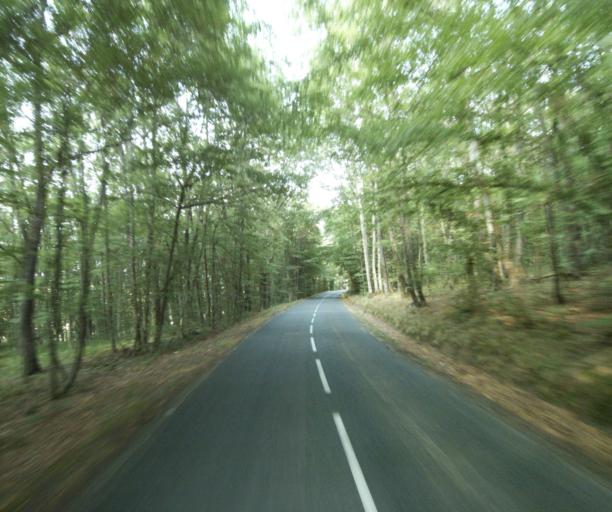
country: FR
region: Rhone-Alpes
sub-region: Departement du Rhone
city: Savigny
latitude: 45.8370
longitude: 4.5596
